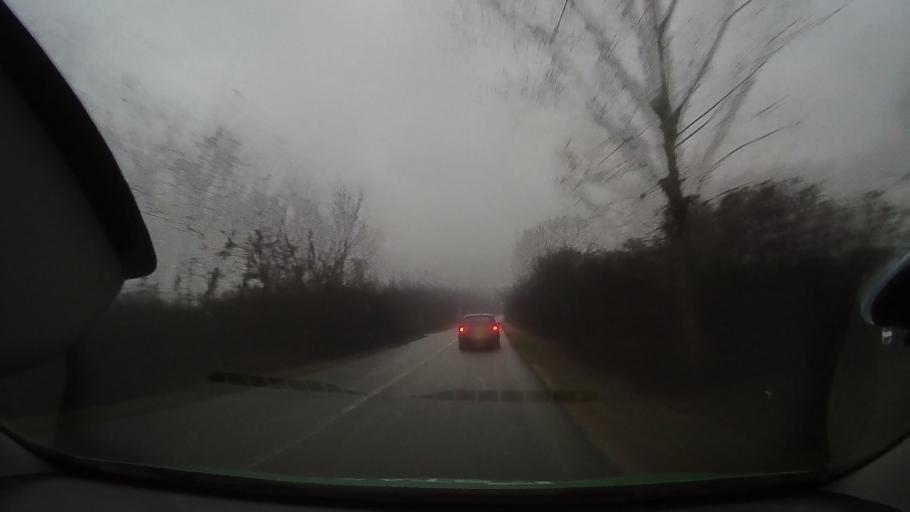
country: RO
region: Arad
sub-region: Comuna Craiova
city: Craiova
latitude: 46.5943
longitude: 21.9776
